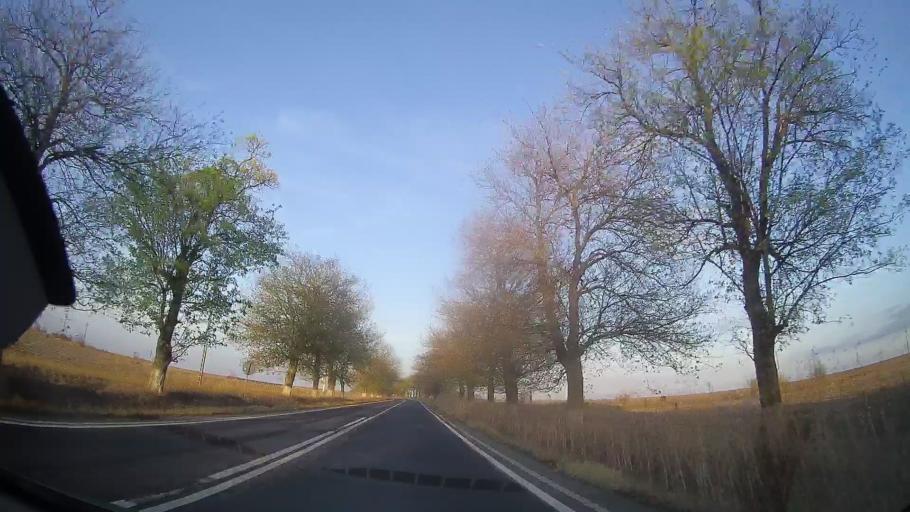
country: RO
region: Constanta
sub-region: Comuna Comana
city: Comana
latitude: 43.9000
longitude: 28.3245
